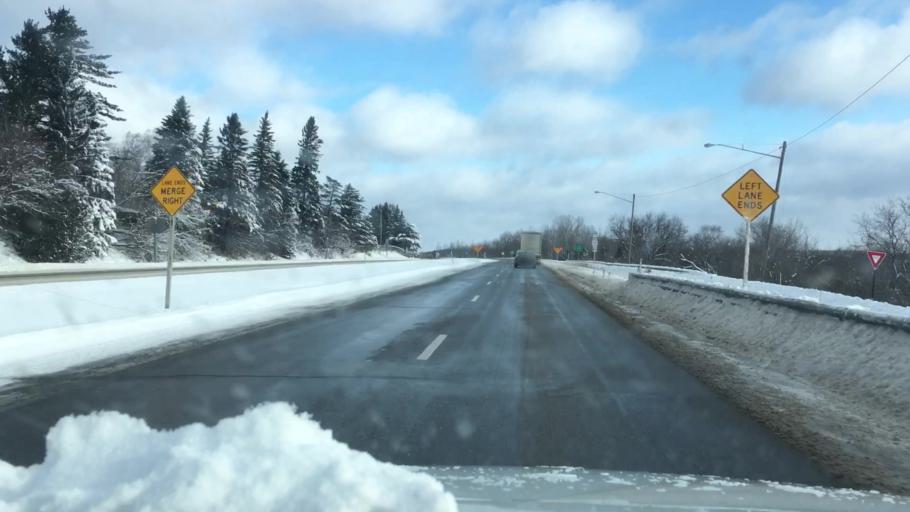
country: US
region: Maine
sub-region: Aroostook County
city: Caribou
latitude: 46.8628
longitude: -68.0015
